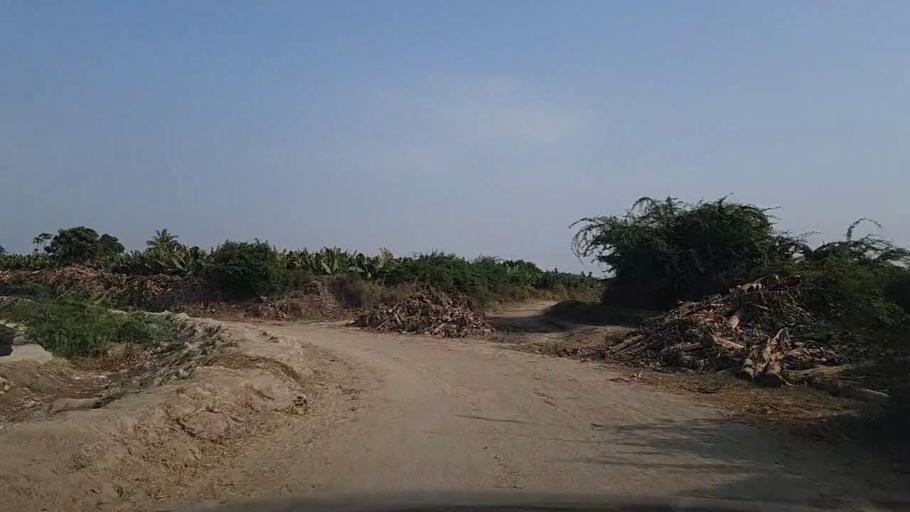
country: PK
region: Sindh
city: Thatta
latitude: 24.6451
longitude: 67.9319
